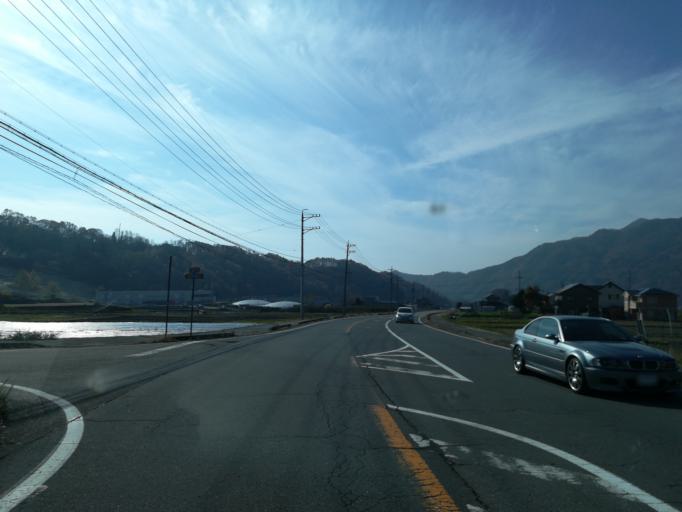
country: JP
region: Nagano
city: Ueda
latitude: 36.4463
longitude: 138.3199
